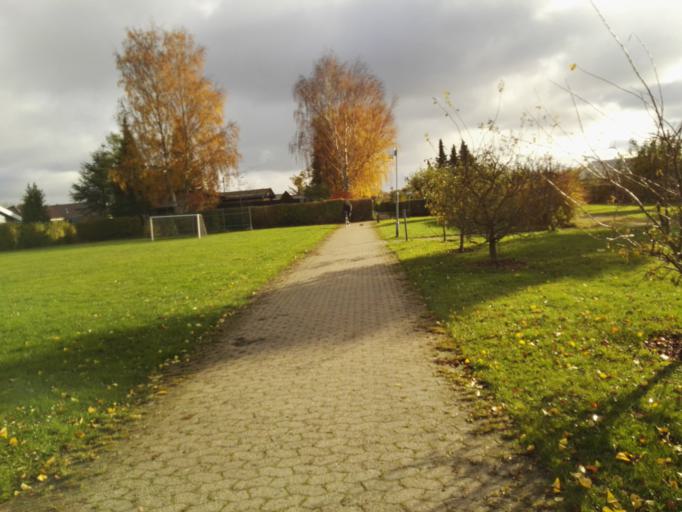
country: DK
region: Capital Region
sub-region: Ballerup Kommune
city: Ballerup
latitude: 55.7115
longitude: 12.3874
